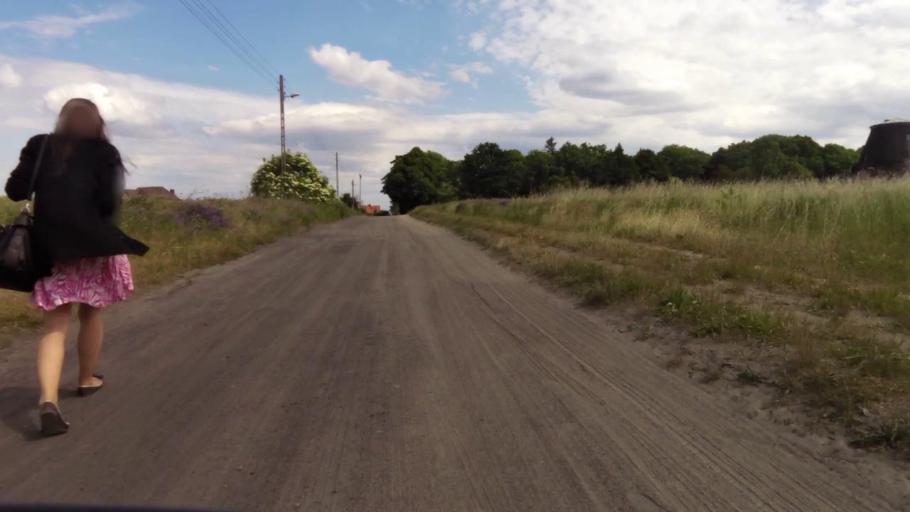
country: PL
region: West Pomeranian Voivodeship
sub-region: Powiat kamienski
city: Wolin
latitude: 53.8433
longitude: 14.6045
